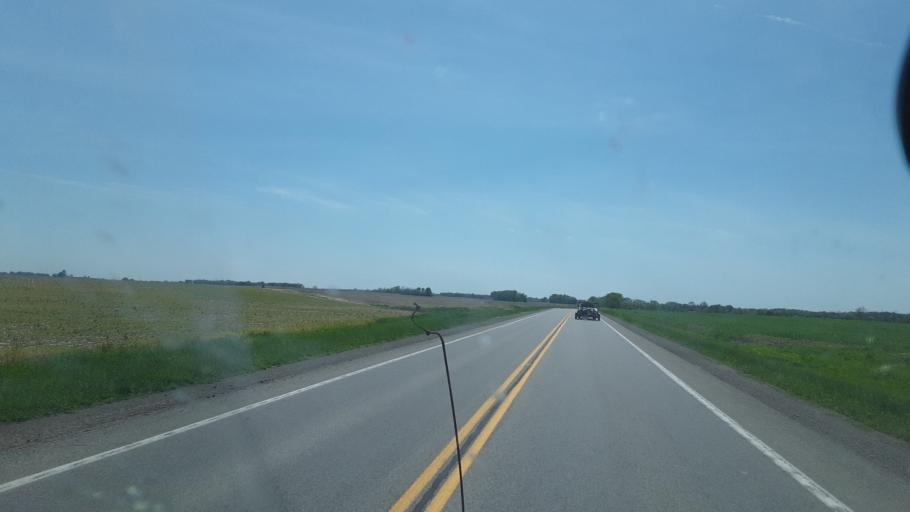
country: US
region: Illinois
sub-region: White County
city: Carmi
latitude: 38.1382
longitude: -88.0918
